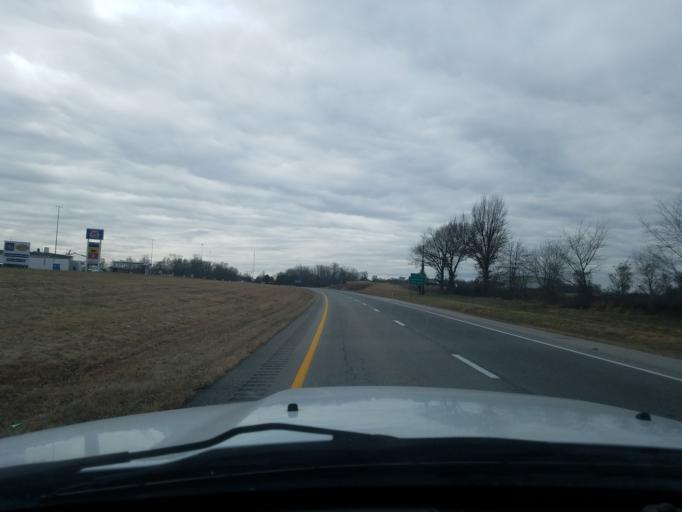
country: US
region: Kentucky
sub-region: Ohio County
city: Beaver Dam
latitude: 37.3779
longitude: -86.8262
